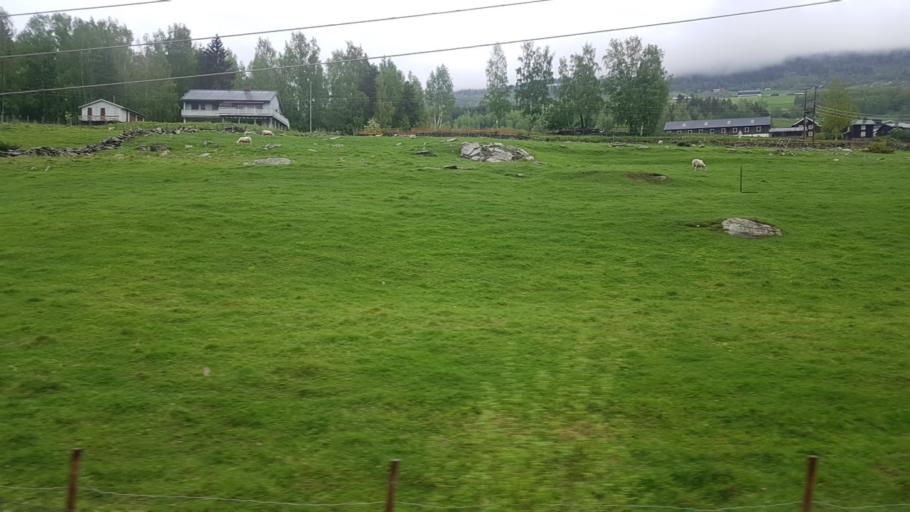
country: NO
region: Oppland
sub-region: Sor-Fron
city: Hundorp
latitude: 61.5540
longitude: 9.9460
